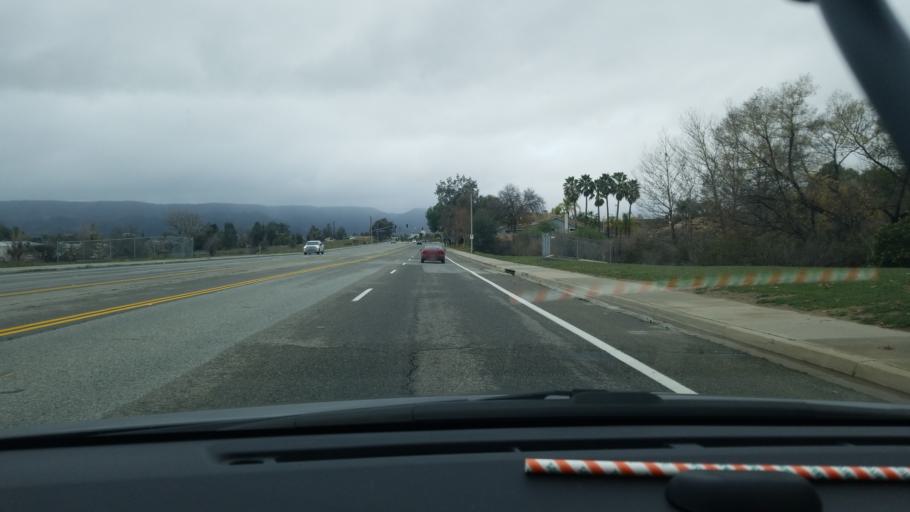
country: US
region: California
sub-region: Riverside County
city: Murrieta
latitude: 33.5638
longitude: -117.1924
